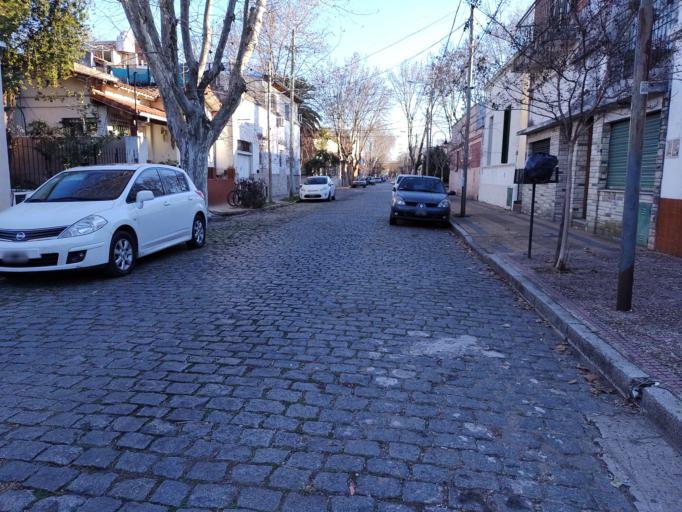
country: AR
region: Buenos Aires
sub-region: Partido de Tigre
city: Tigre
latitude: -34.4501
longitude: -58.5473
